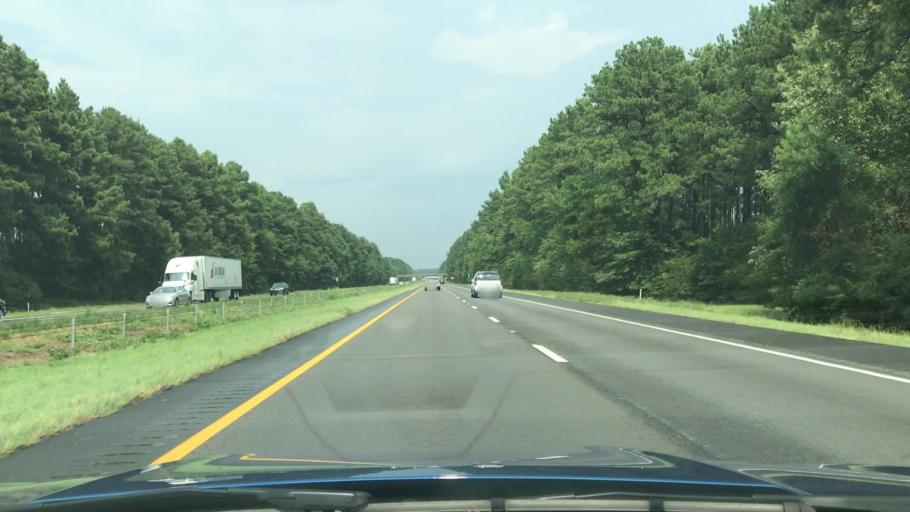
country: US
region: Texas
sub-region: Harrison County
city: Hallsville
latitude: 32.4786
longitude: -94.5530
